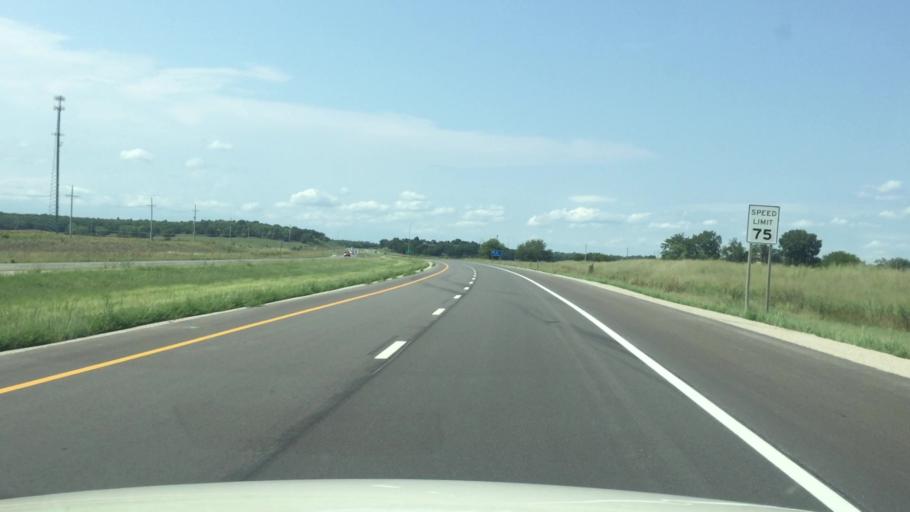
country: US
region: Kansas
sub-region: Linn County
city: La Cygne
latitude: 38.3348
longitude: -94.6778
